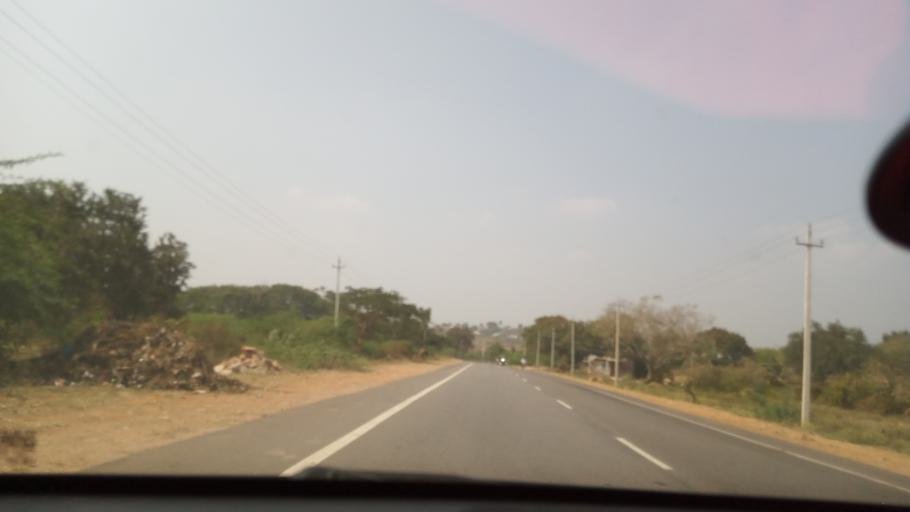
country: IN
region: Karnataka
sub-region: Mysore
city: Nanjangud
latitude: 12.0866
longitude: 76.7299
